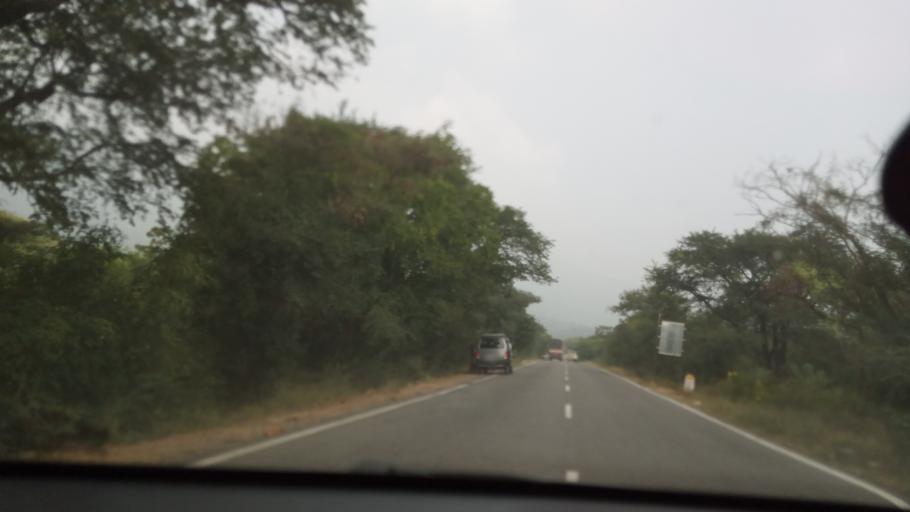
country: IN
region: Tamil Nadu
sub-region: Erode
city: Sathyamangalam
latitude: 11.5708
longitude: 77.1346
